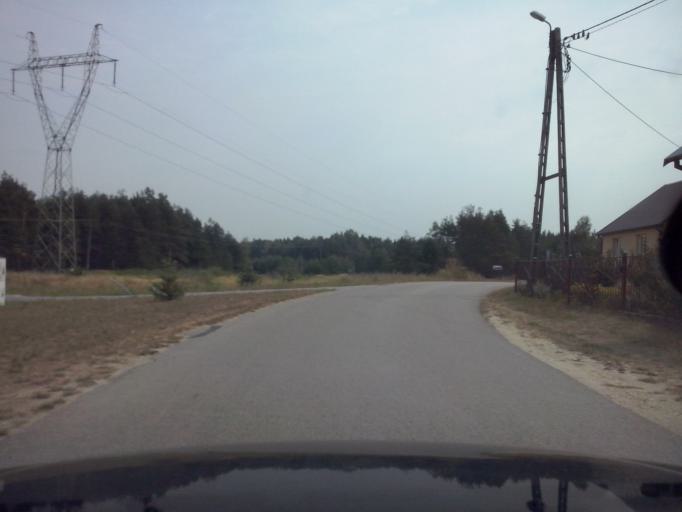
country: PL
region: Swietokrzyskie
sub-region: Powiat kielecki
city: Brzeziny
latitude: 50.7477
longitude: 20.5618
